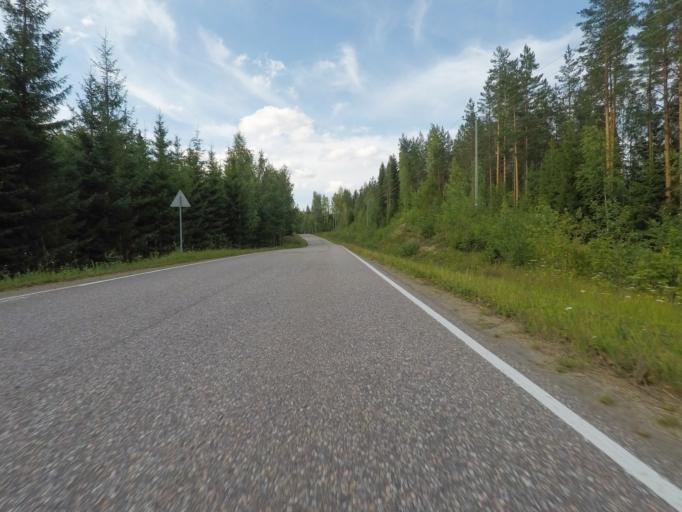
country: FI
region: Southern Savonia
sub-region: Savonlinna
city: Sulkava
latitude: 61.7325
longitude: 28.2101
